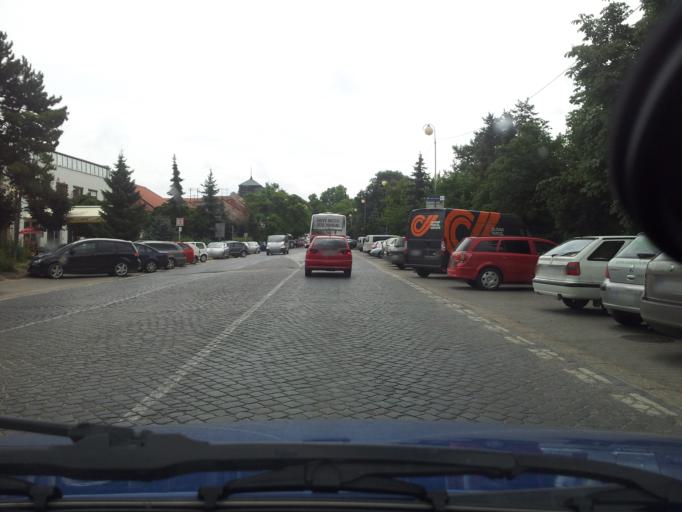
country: SK
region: Nitriansky
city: Zlate Moravce
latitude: 48.3848
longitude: 18.3920
